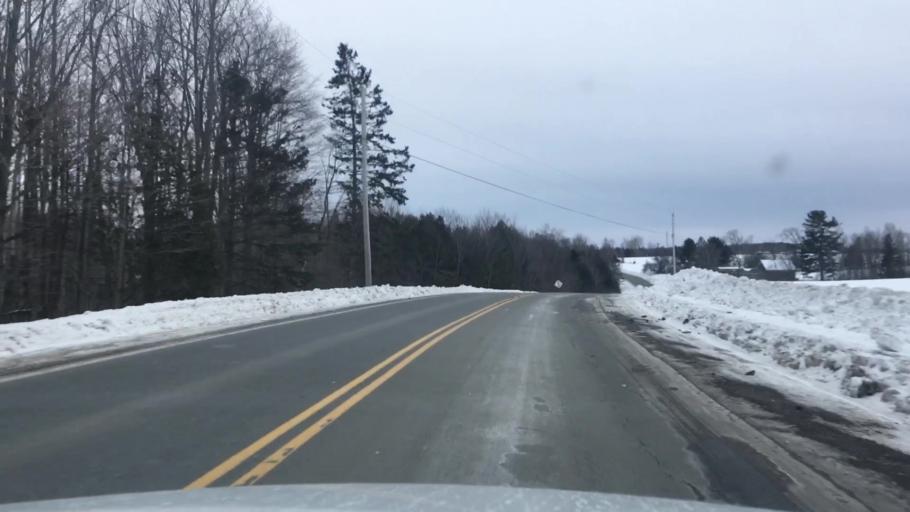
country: US
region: Maine
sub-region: Penobscot County
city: Corinna
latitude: 44.9542
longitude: -69.2025
